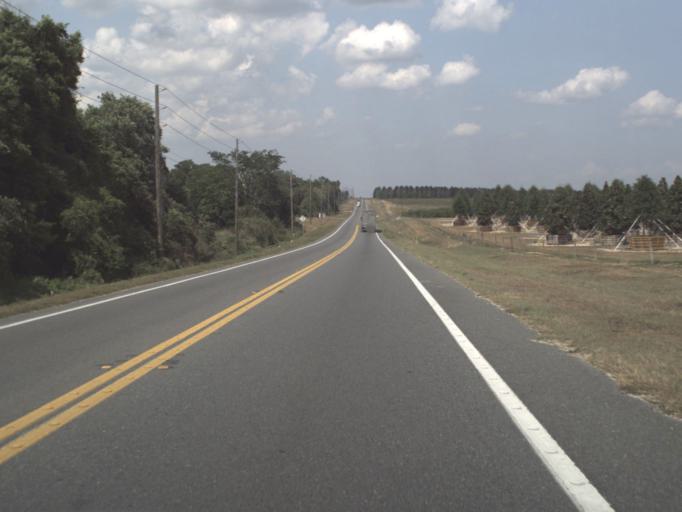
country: US
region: Florida
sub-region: Lake County
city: Groveland
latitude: 28.5966
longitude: -81.8434
